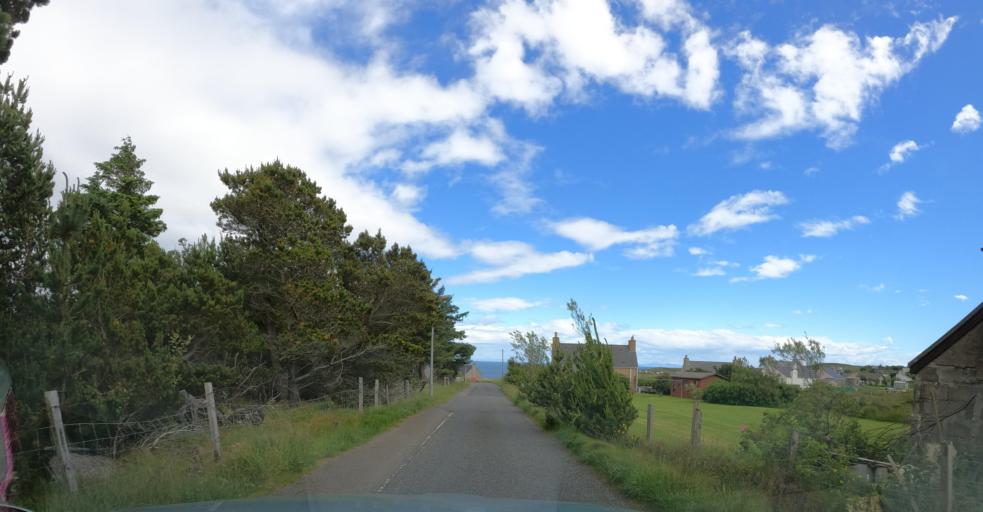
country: GB
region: Scotland
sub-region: Eilean Siar
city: Stornoway
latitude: 58.2007
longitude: -6.2260
